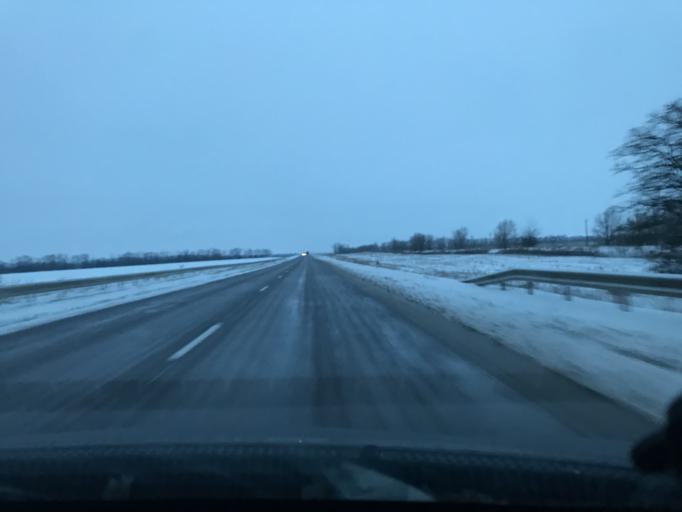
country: RU
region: Rostov
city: Letnik
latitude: 45.9824
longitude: 41.2384
